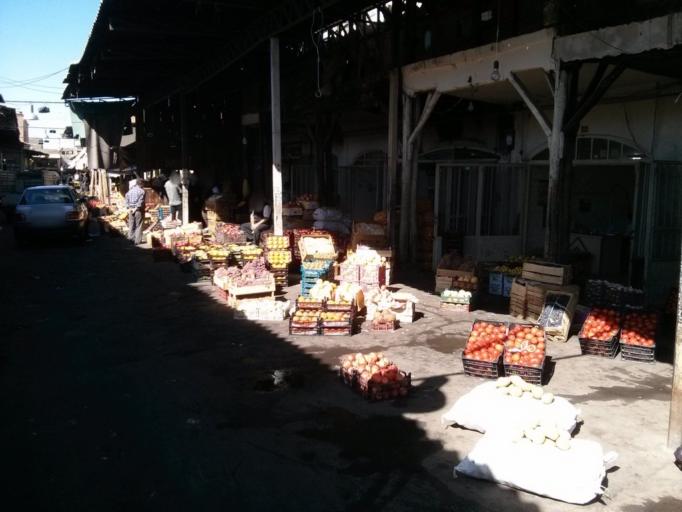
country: IR
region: East Azerbaijan
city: Tabriz
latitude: 38.0847
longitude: 46.2945
